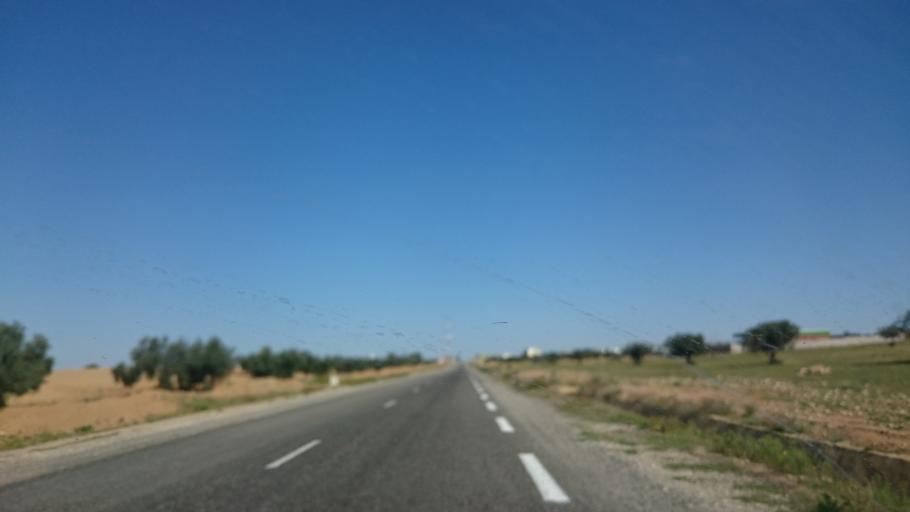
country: TN
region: Safaqis
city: Sfax
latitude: 34.8086
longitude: 10.4809
